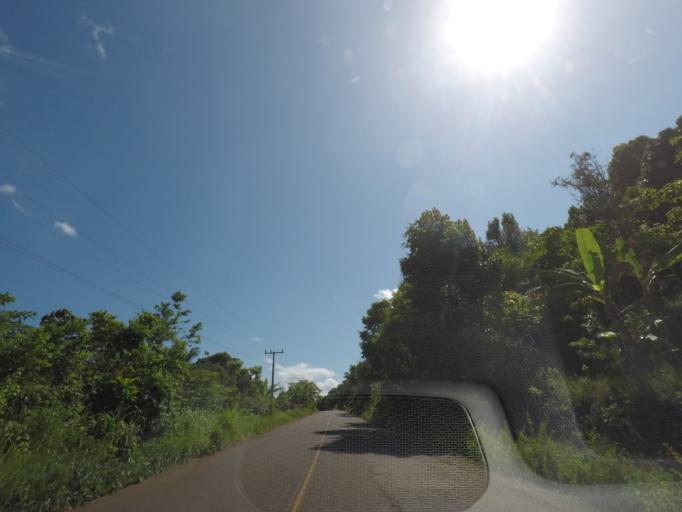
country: BR
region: Bahia
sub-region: Itubera
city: Itubera
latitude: -13.7095
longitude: -39.1401
